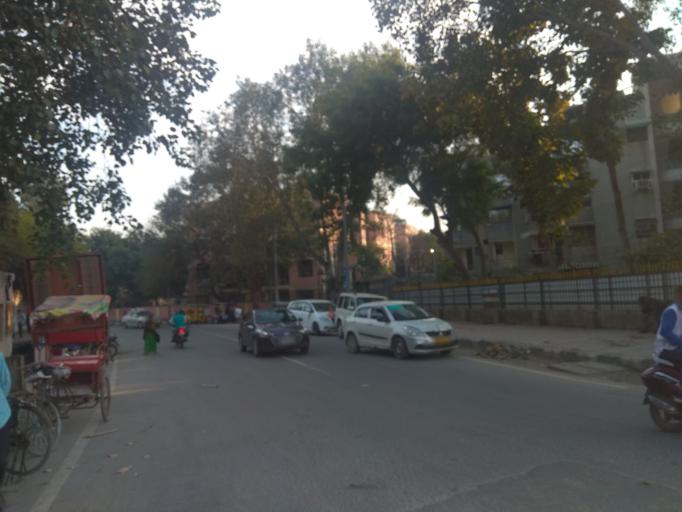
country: IN
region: NCT
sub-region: West Delhi
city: Nangloi Jat
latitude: 28.6409
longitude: 77.0641
